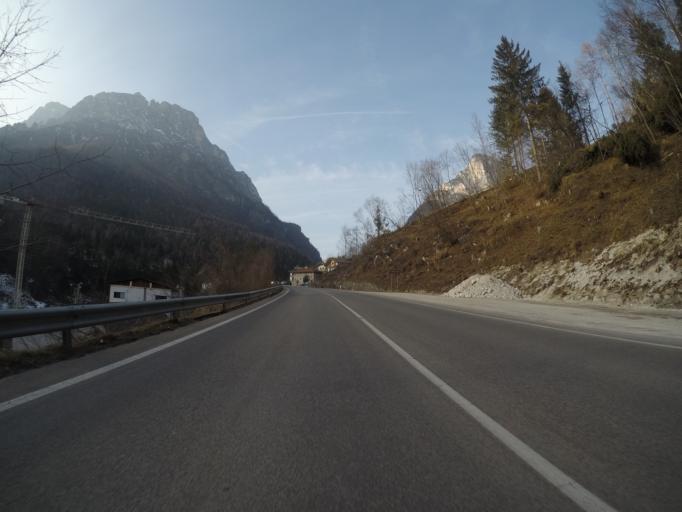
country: IT
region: Veneto
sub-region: Provincia di Belluno
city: Taibon Agordino
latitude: 46.3077
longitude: 12.0116
